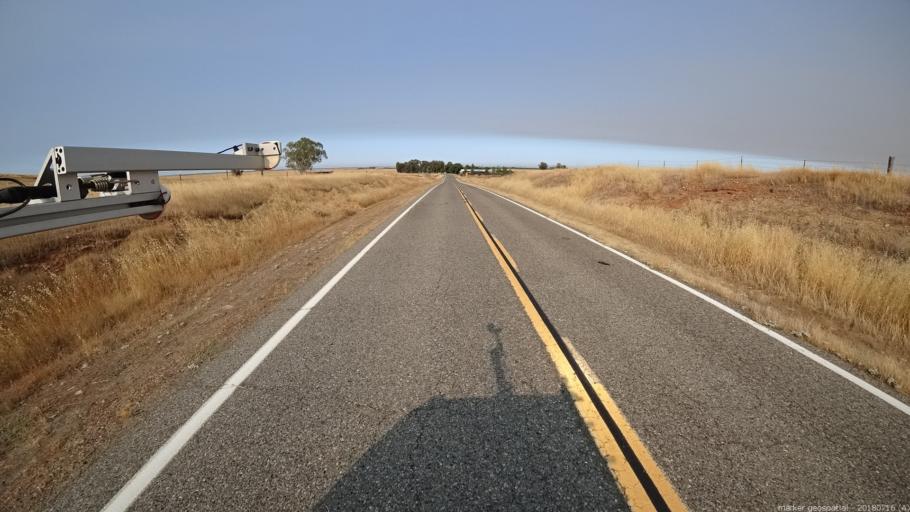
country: US
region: California
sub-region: Madera County
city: Madera Acres
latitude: 37.1424
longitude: -120.0161
